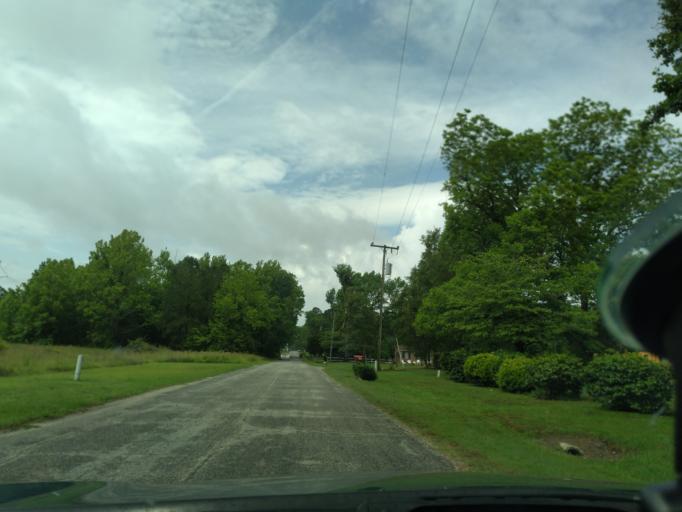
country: US
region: North Carolina
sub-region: Chowan County
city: Edenton
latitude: 35.9335
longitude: -76.6107
